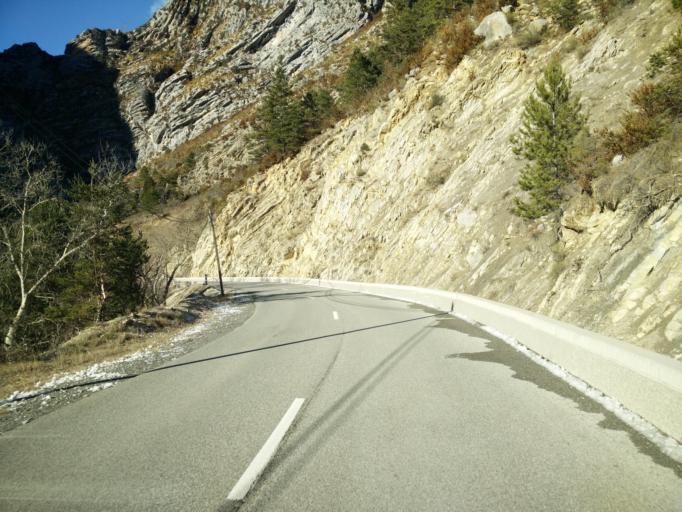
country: FR
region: Provence-Alpes-Cote d'Azur
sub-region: Departement des Alpes-de-Haute-Provence
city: Castellane
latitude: 43.8313
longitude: 6.4524
